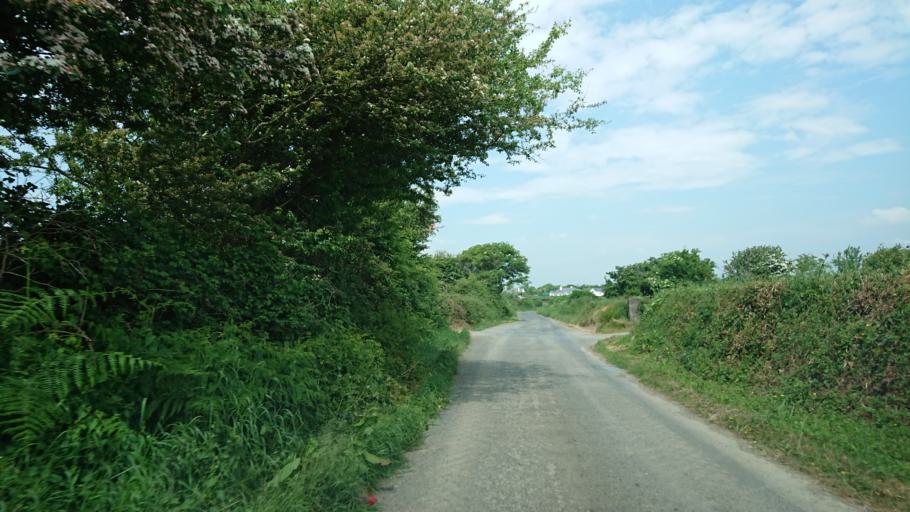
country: IE
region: Munster
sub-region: Waterford
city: Dunmore East
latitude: 52.2123
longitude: -6.9954
